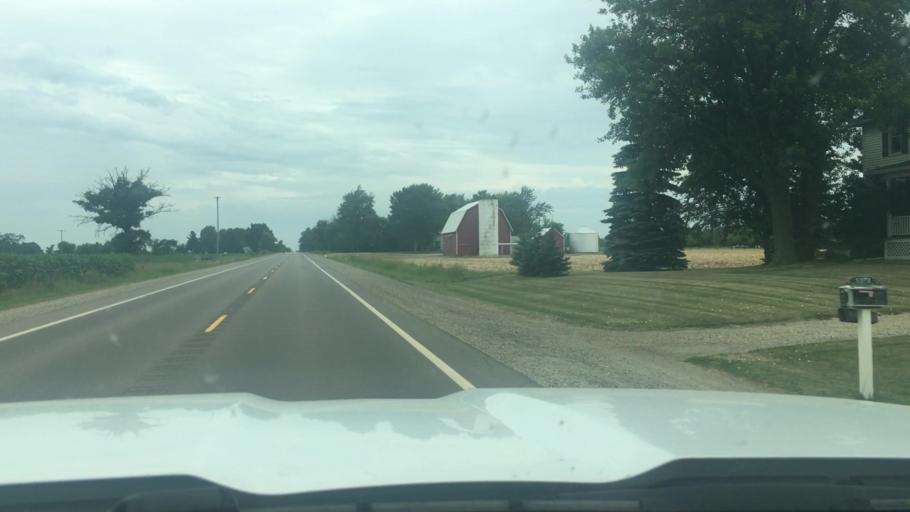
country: US
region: Michigan
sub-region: Clinton County
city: Saint Johns
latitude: 43.0016
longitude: -84.6275
